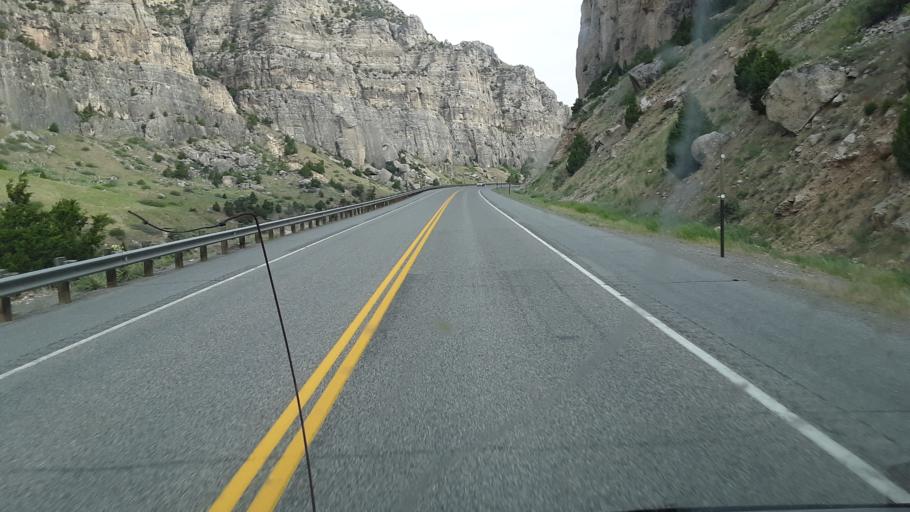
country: US
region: Wyoming
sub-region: Hot Springs County
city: Thermopolis
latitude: 43.5287
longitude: -108.1766
